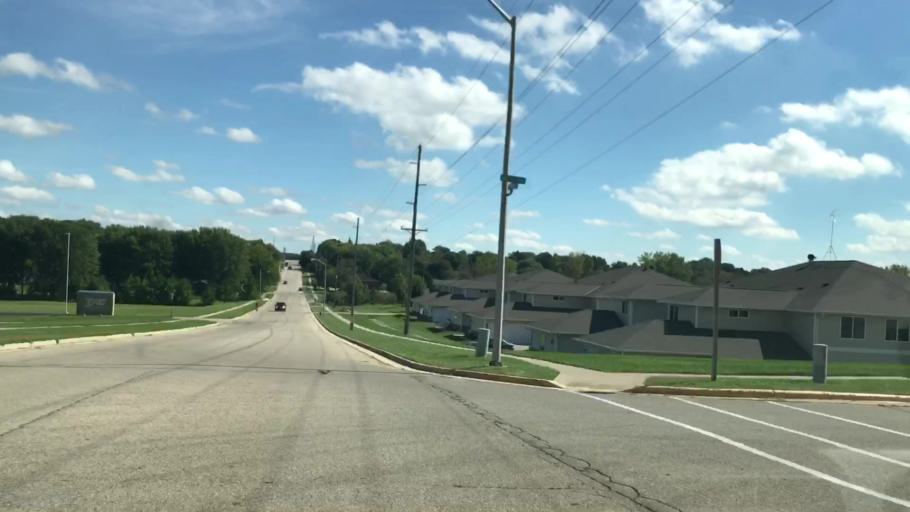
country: US
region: Wisconsin
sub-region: Dodge County
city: Mayville
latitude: 43.5012
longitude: -88.5640
